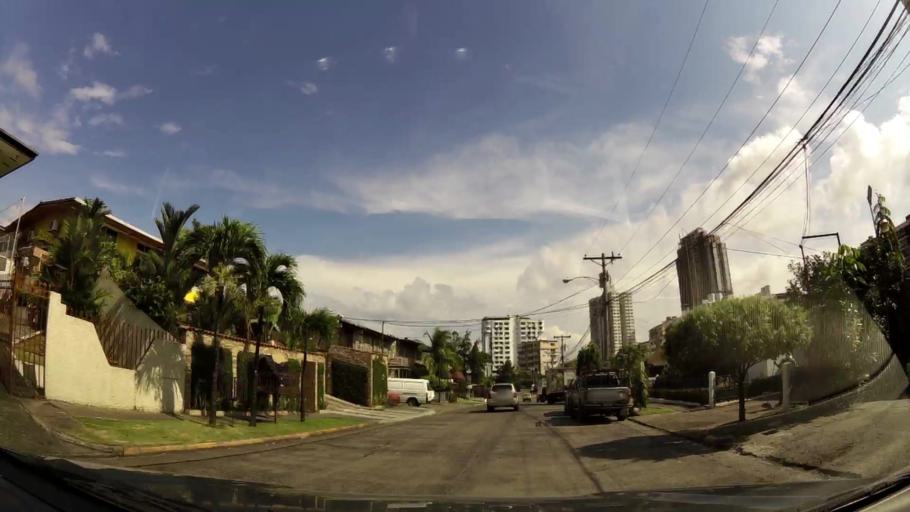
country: PA
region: Panama
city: Panama
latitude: 8.9945
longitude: -79.5214
